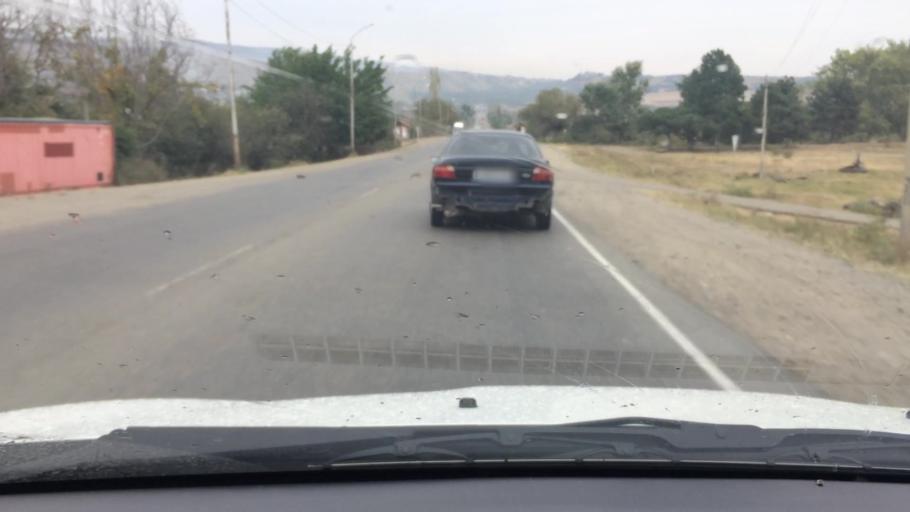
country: GE
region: T'bilisi
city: Tbilisi
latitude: 41.6034
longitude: 44.7799
